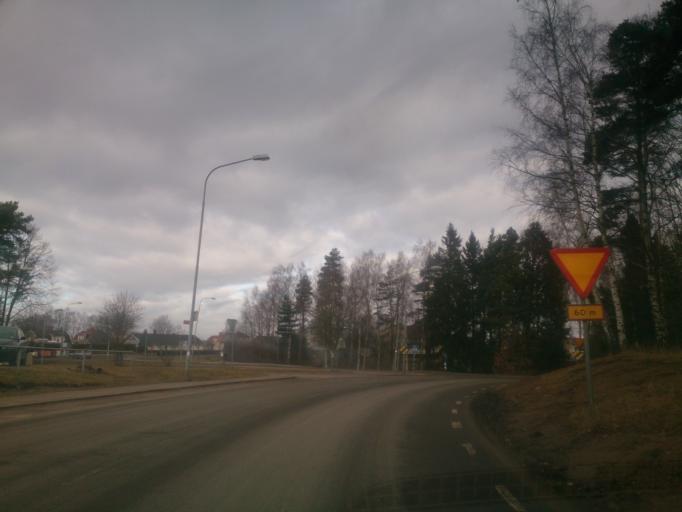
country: SE
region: OEstergoetland
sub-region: Motala Kommun
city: Motala
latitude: 58.5247
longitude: 15.0570
